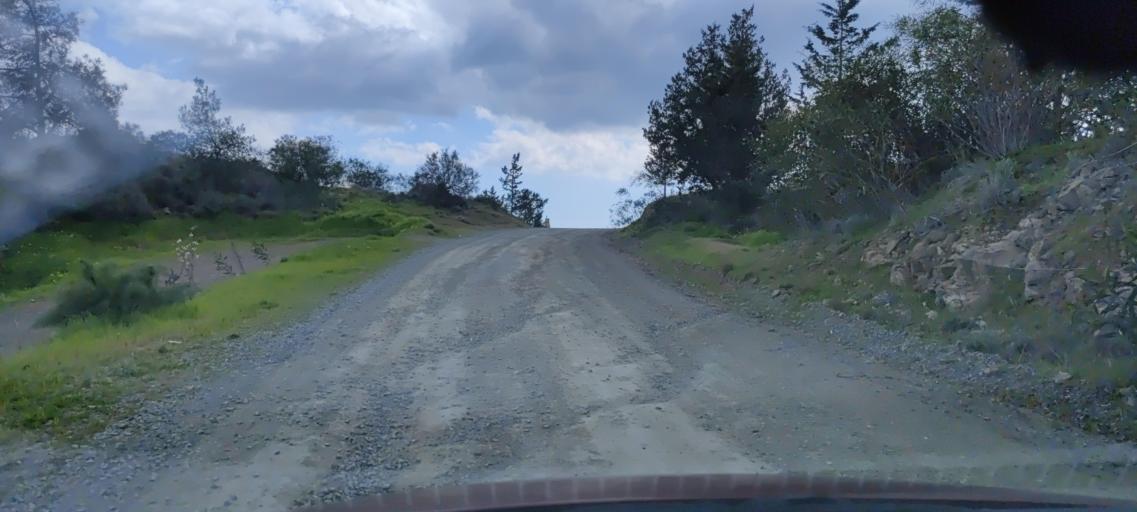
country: CY
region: Larnaka
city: Kornos
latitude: 34.9097
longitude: 33.4009
